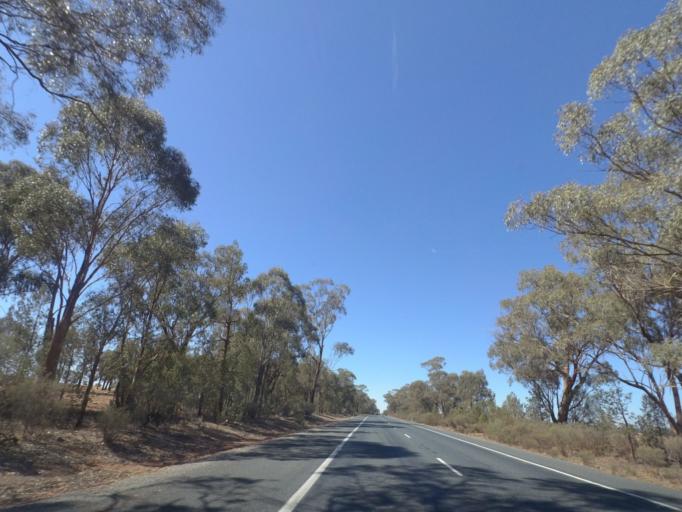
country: AU
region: New South Wales
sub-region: Bland
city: West Wyalong
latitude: -34.2101
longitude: 147.1089
